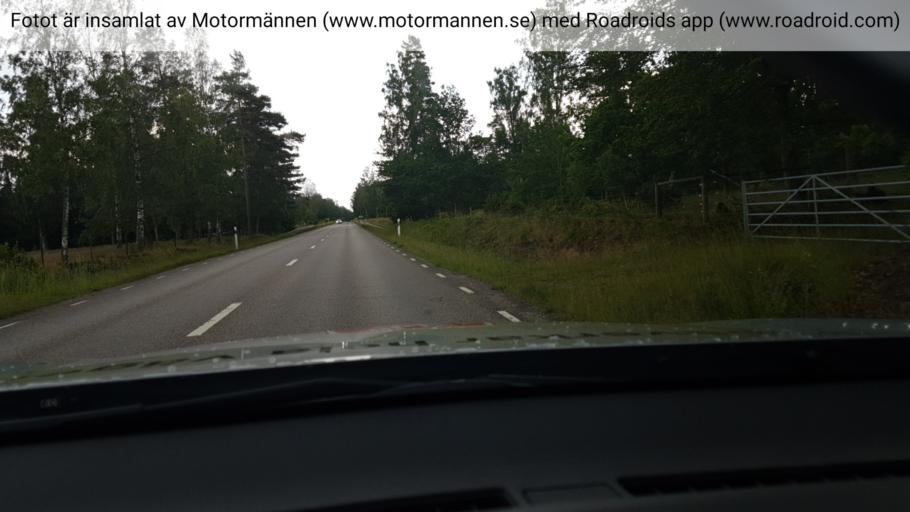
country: SE
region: Vaestra Goetaland
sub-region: Hjo Kommun
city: Hjo
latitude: 58.1688
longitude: 14.2071
